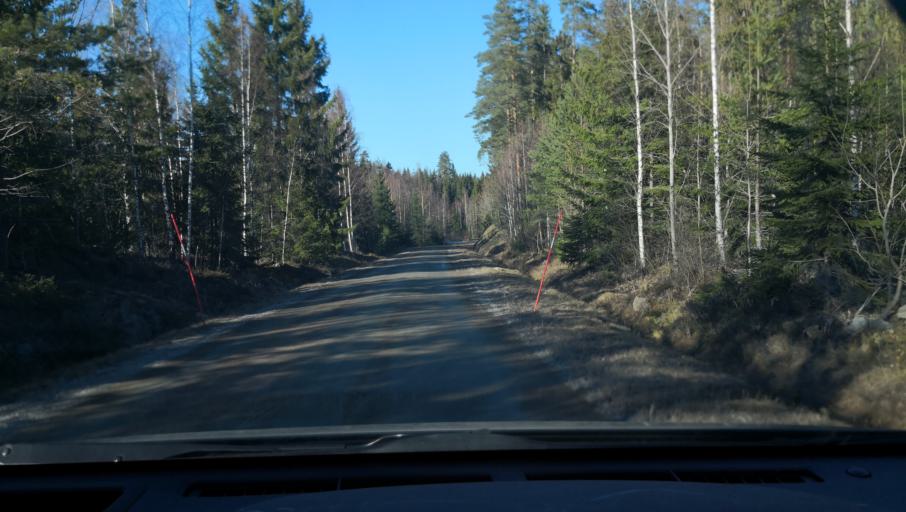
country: SE
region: Vaestmanland
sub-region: Sala Kommun
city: Sala
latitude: 60.1614
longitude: 16.6284
